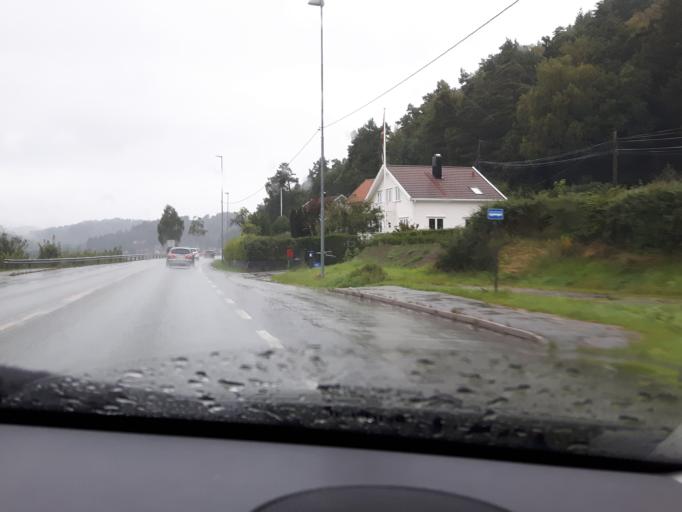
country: NO
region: Vest-Agder
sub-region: Mandal
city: Mandal
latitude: 58.0428
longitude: 7.4212
